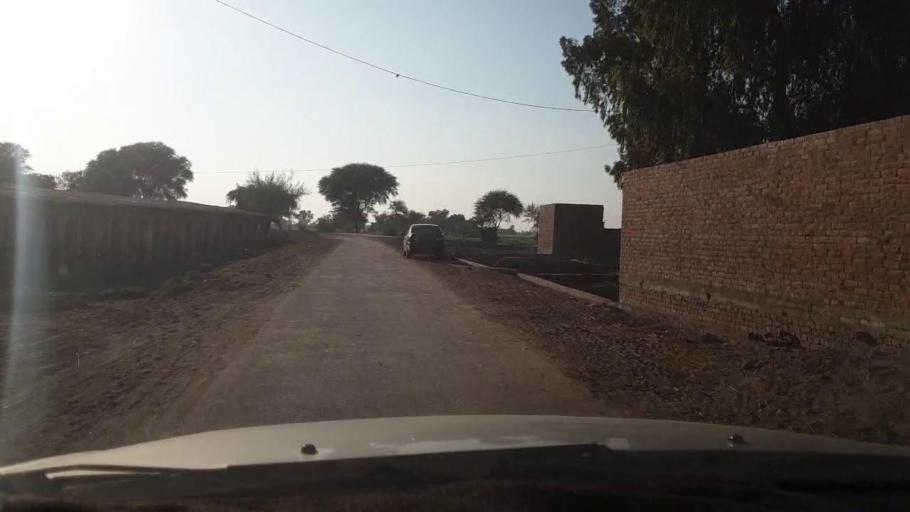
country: PK
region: Sindh
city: Mirpur Mathelo
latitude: 28.0128
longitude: 69.5430
